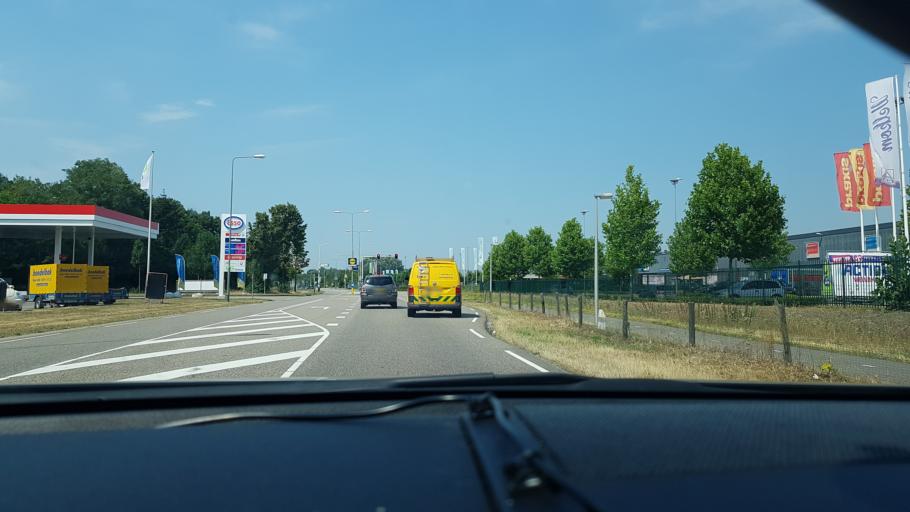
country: NL
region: Limburg
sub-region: Gemeente Roermond
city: Leeuwen
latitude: 51.1999
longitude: 6.0264
